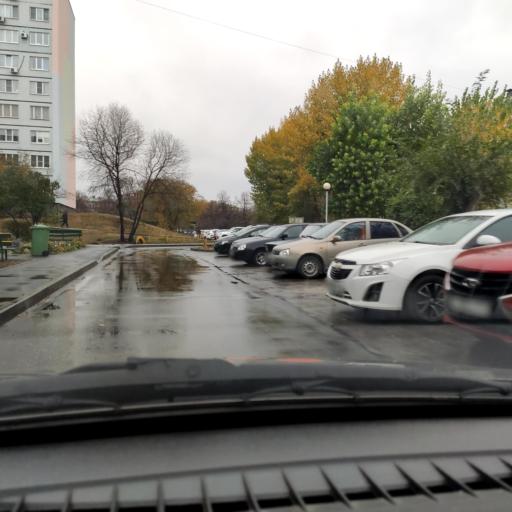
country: RU
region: Samara
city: Tol'yatti
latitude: 53.5207
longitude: 49.2880
